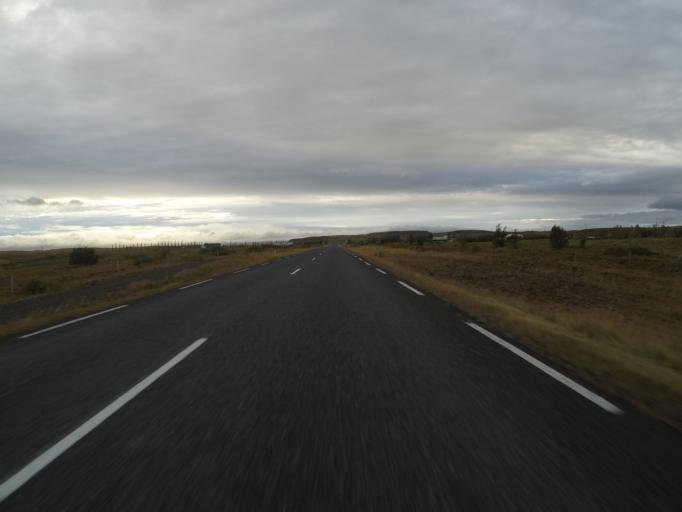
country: IS
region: South
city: Vestmannaeyjar
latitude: 64.0410
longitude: -20.2388
